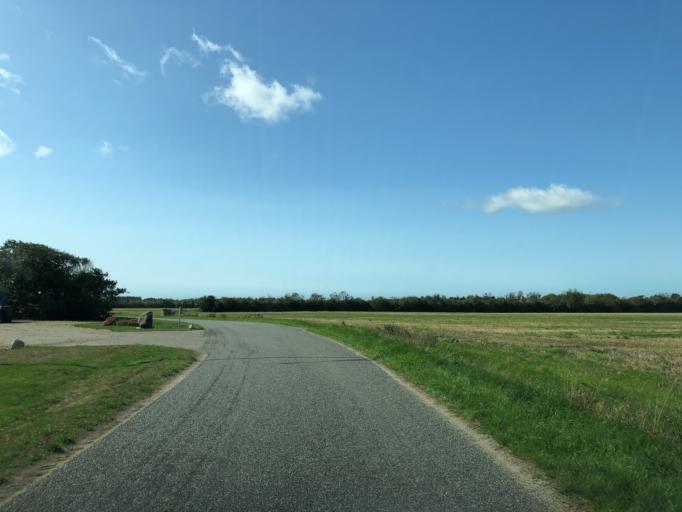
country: DK
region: Central Jutland
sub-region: Holstebro Kommune
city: Ulfborg
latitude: 56.2623
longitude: 8.1720
